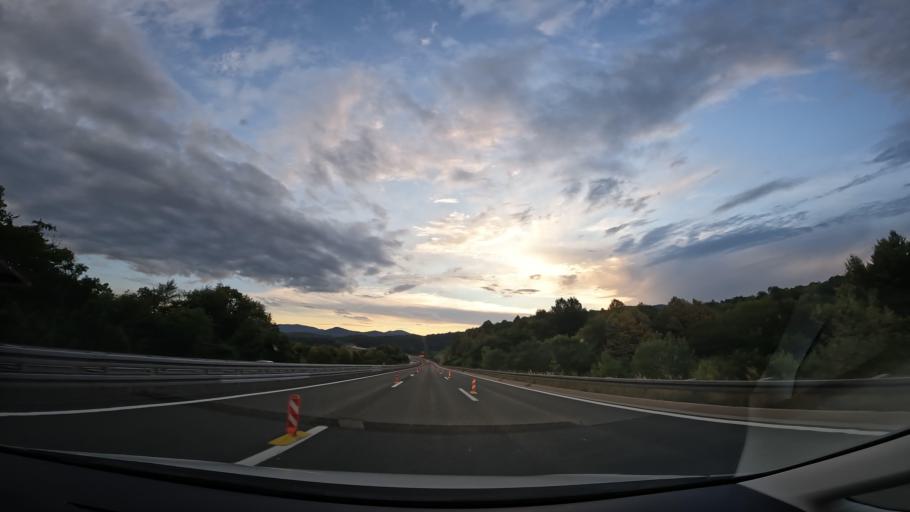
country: HR
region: Primorsko-Goranska
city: Vrbovsko
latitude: 45.3772
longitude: 15.1460
